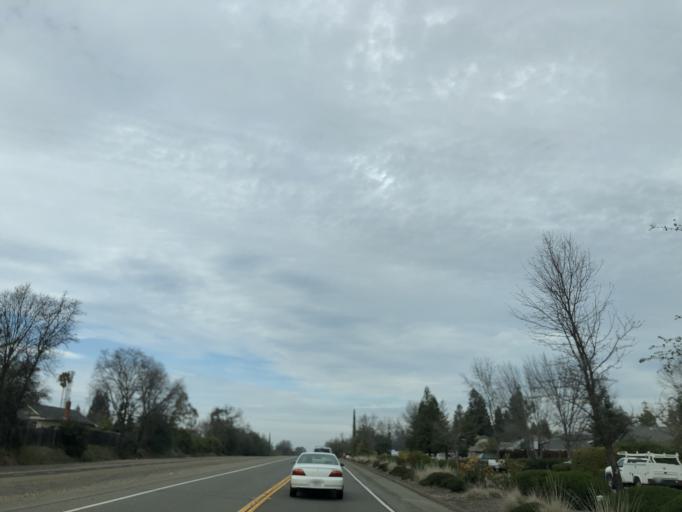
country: US
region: California
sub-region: El Dorado County
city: El Dorado Hills
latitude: 38.6898
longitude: -121.0809
